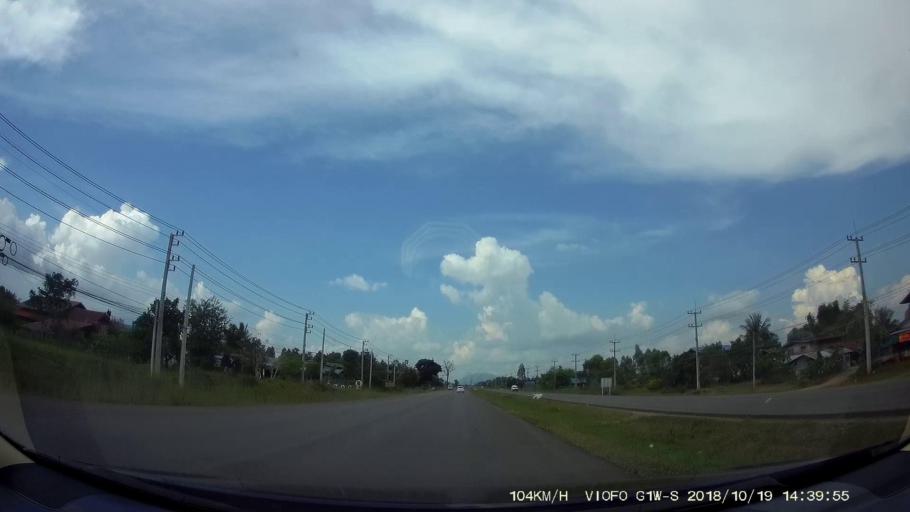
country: TH
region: Chaiyaphum
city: Kaeng Khro
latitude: 16.2330
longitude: 102.1951
